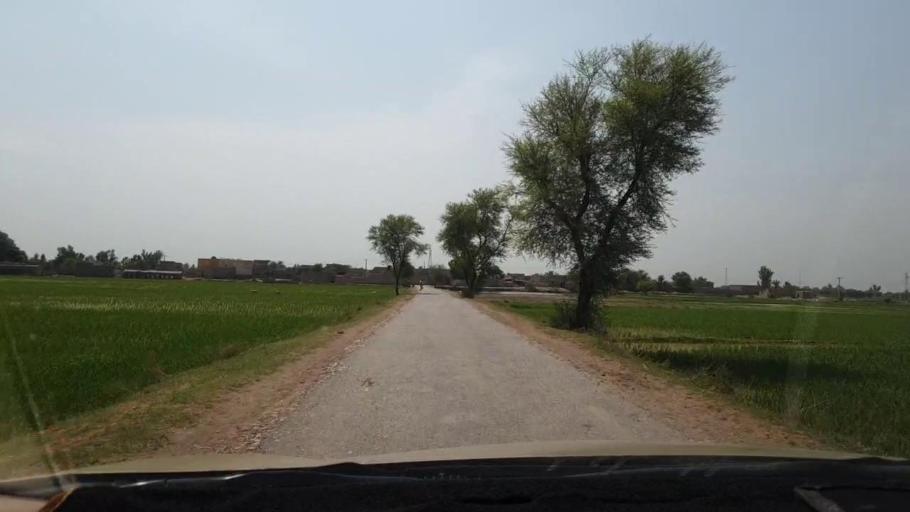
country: PK
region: Sindh
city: Naudero
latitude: 27.6351
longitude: 68.2740
